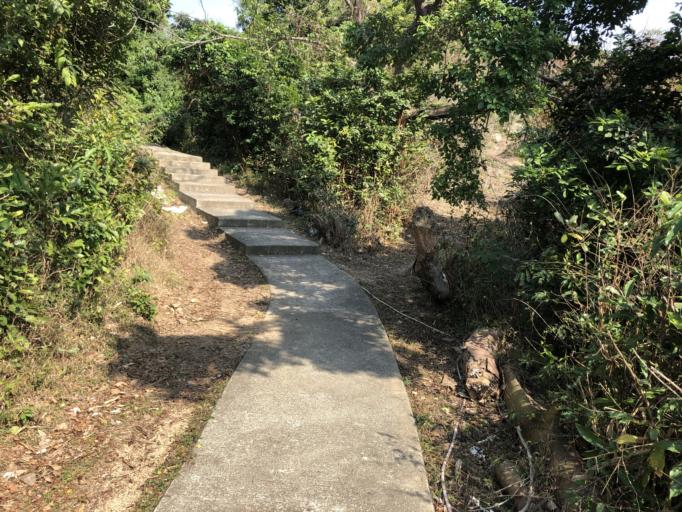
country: HK
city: Sok Kwu Wan
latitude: 22.1637
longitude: 114.2545
